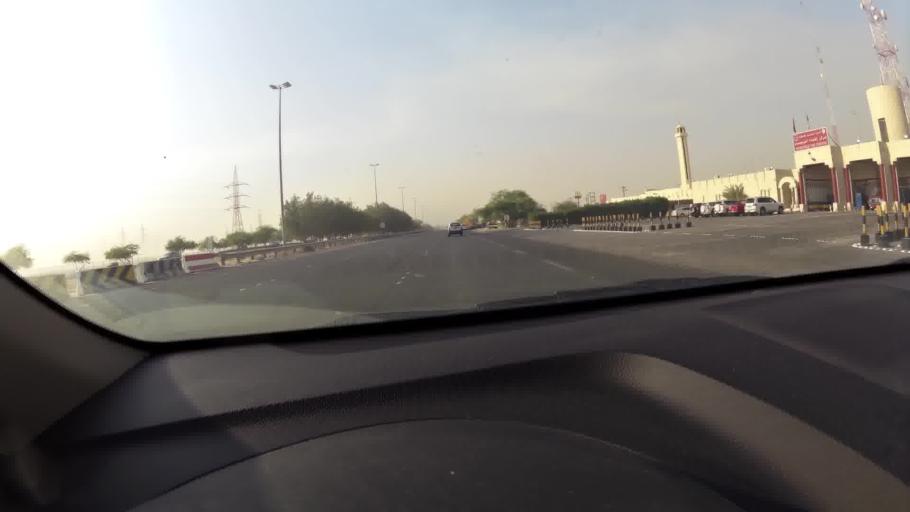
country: SA
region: Eastern Province
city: Al Khafji
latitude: 28.7336
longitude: 48.2854
